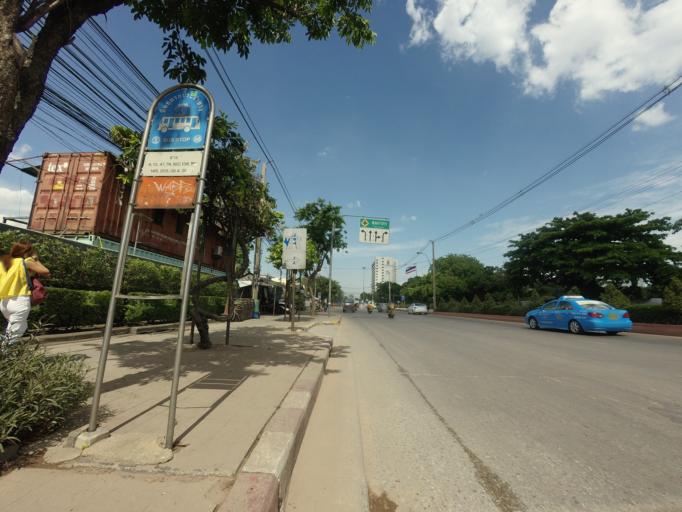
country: TH
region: Bangkok
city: Khlong Toei
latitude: 13.7153
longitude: 100.5638
